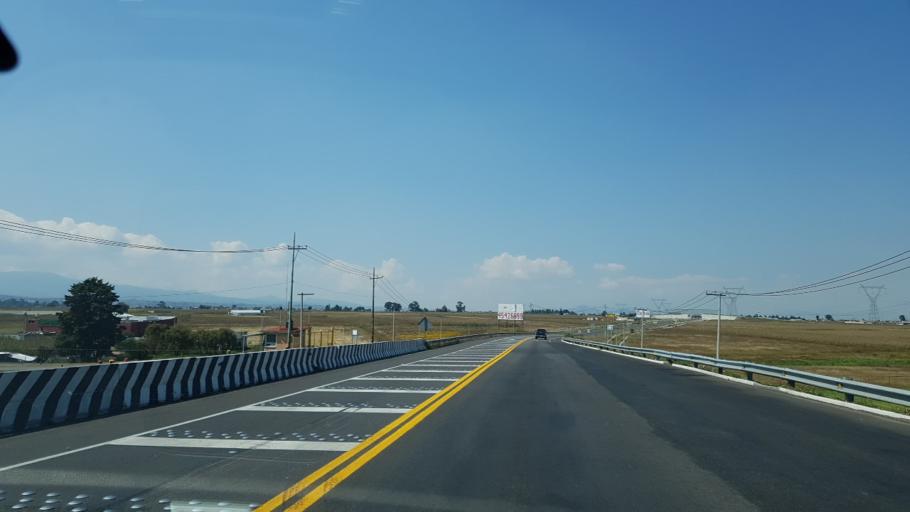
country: MX
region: Mexico
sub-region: Toluca
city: Sebastian Lerdo de Tejada
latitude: 19.3866
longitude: -99.7111
